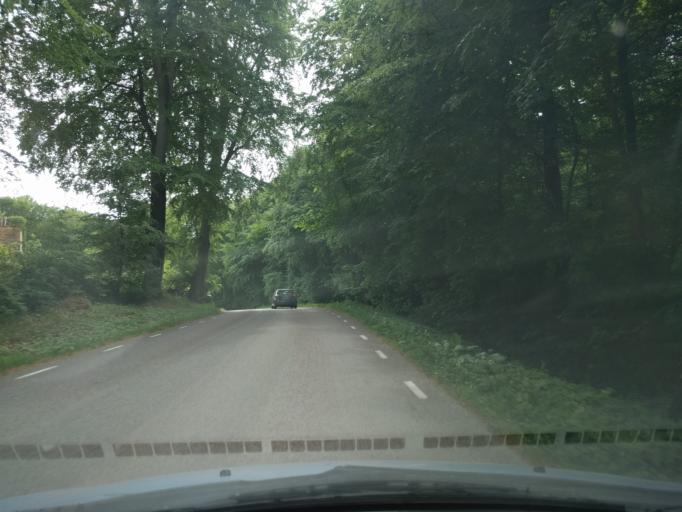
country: SE
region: Skane
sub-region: Svedala Kommun
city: Svedala
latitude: 55.5533
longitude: 13.2078
